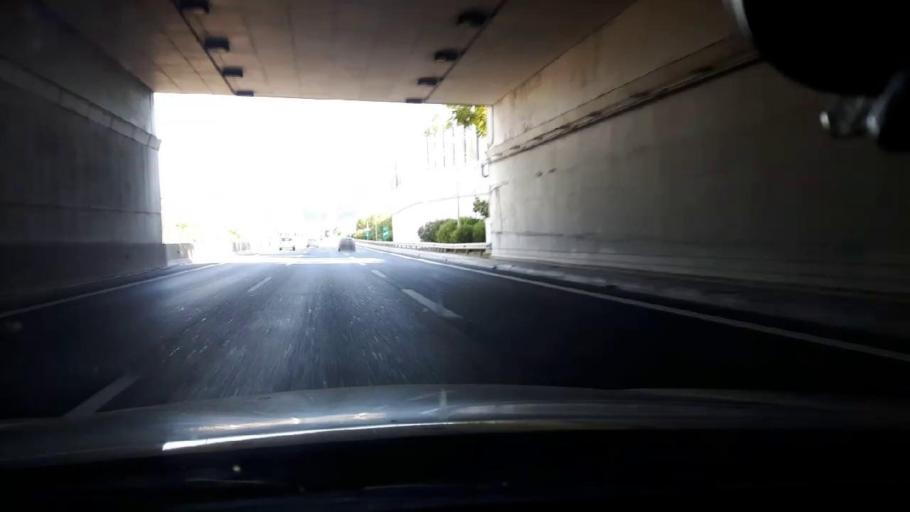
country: GR
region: Attica
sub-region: Nomarchia Anatolikis Attikis
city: Pallini
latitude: 37.9899
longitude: 23.8716
